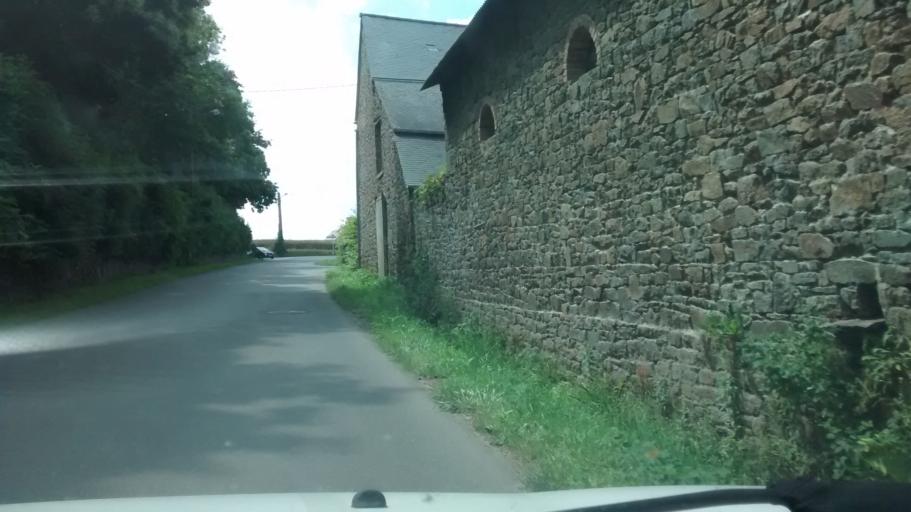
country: FR
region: Brittany
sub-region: Departement d'Ille-et-Vilaine
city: La Gouesniere
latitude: 48.5994
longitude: -1.8947
